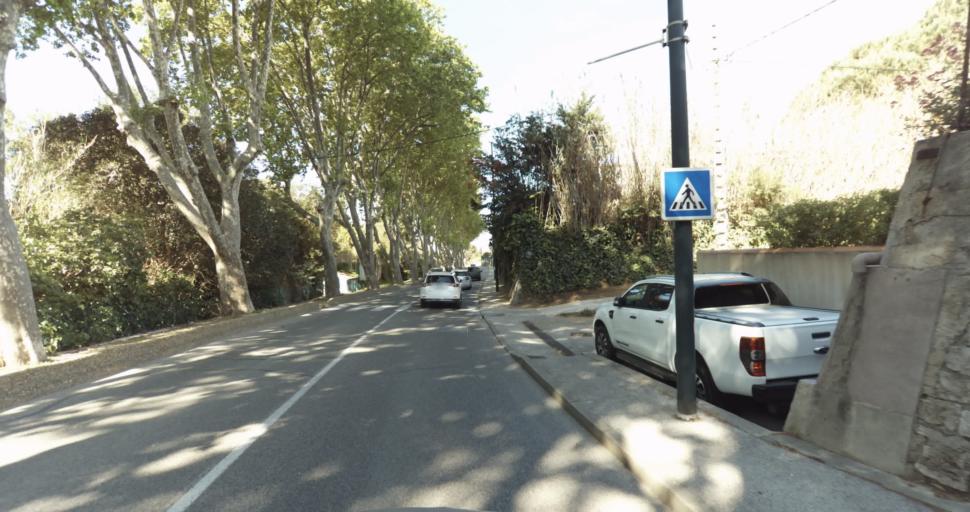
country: FR
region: Provence-Alpes-Cote d'Azur
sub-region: Departement du Var
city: Six-Fours-les-Plages
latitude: 43.1081
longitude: 5.8262
